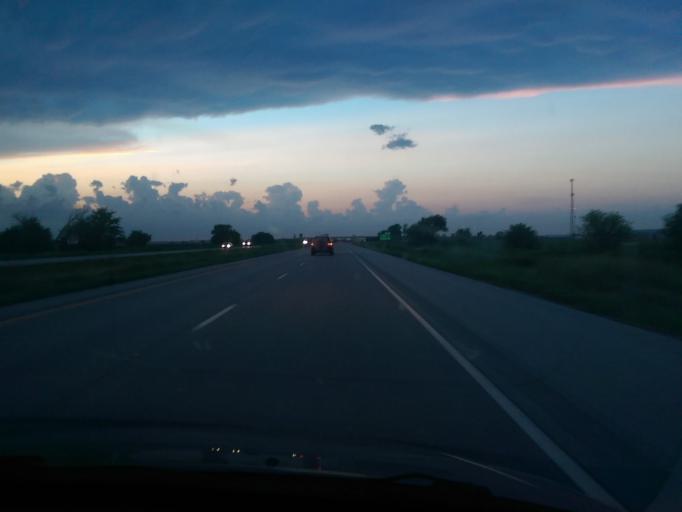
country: US
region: Nebraska
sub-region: Otoe County
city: Nebraska City
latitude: 40.7499
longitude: -95.8175
